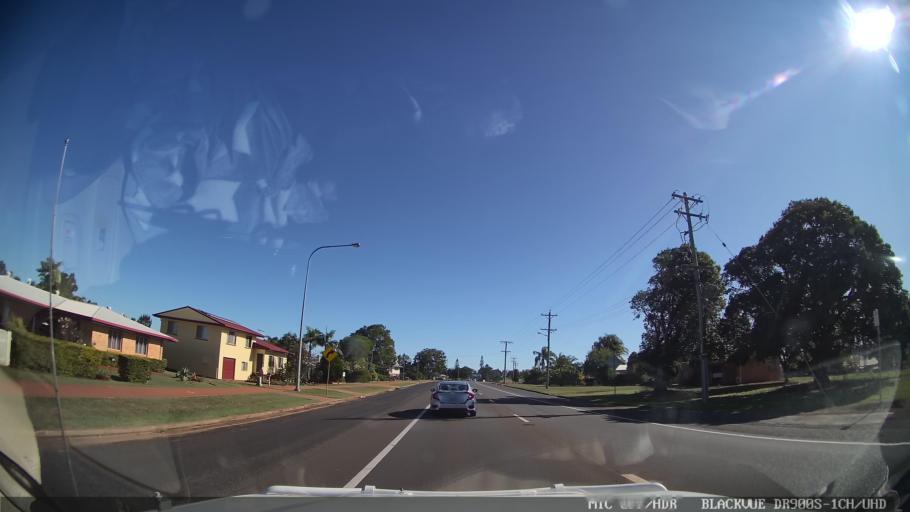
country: AU
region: Queensland
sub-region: Bundaberg
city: Childers
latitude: -25.2332
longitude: 152.2696
